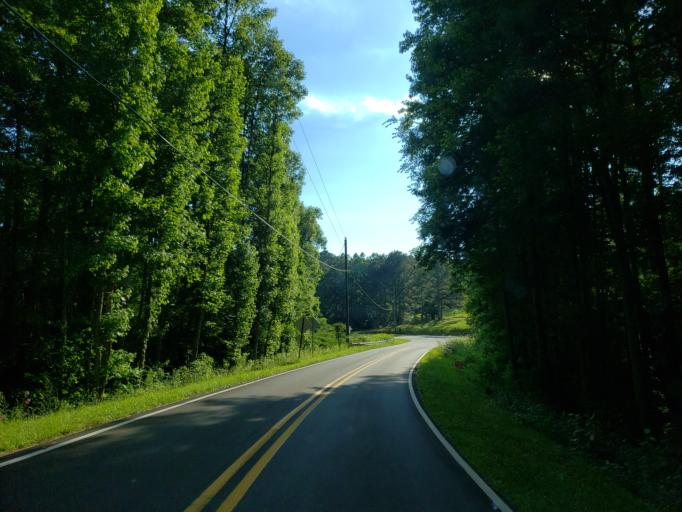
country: US
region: Georgia
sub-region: Haralson County
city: Buchanan
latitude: 33.8557
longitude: -85.2084
